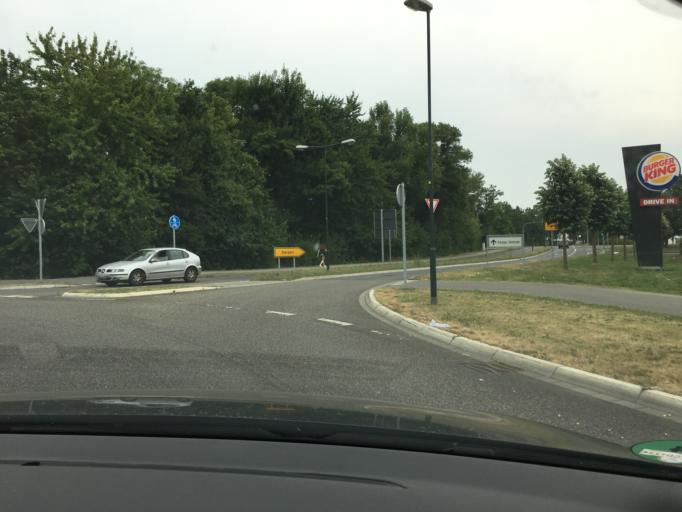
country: DE
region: North Rhine-Westphalia
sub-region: Regierungsbezirk Koln
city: Kerpen
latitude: 50.8821
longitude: 6.6947
